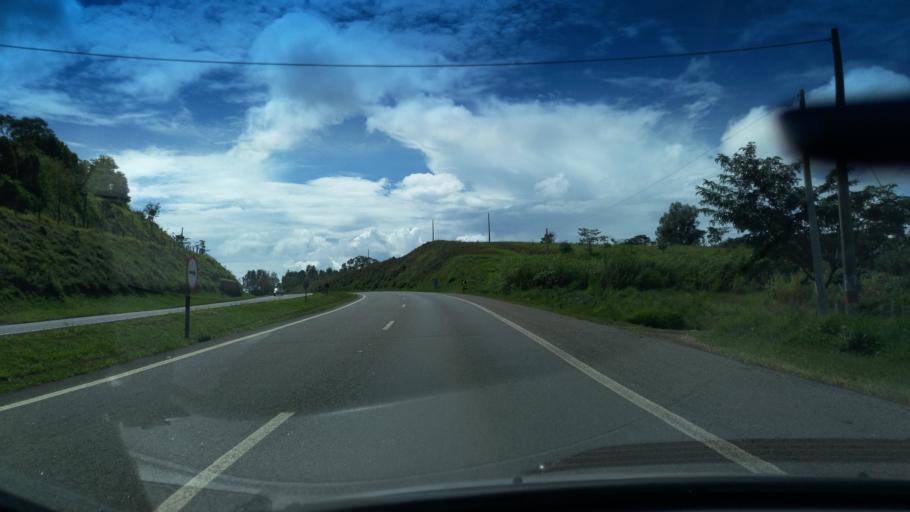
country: BR
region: Sao Paulo
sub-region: Santo Antonio Do Jardim
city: Espirito Santo do Pinhal
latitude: -22.2091
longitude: -46.7810
